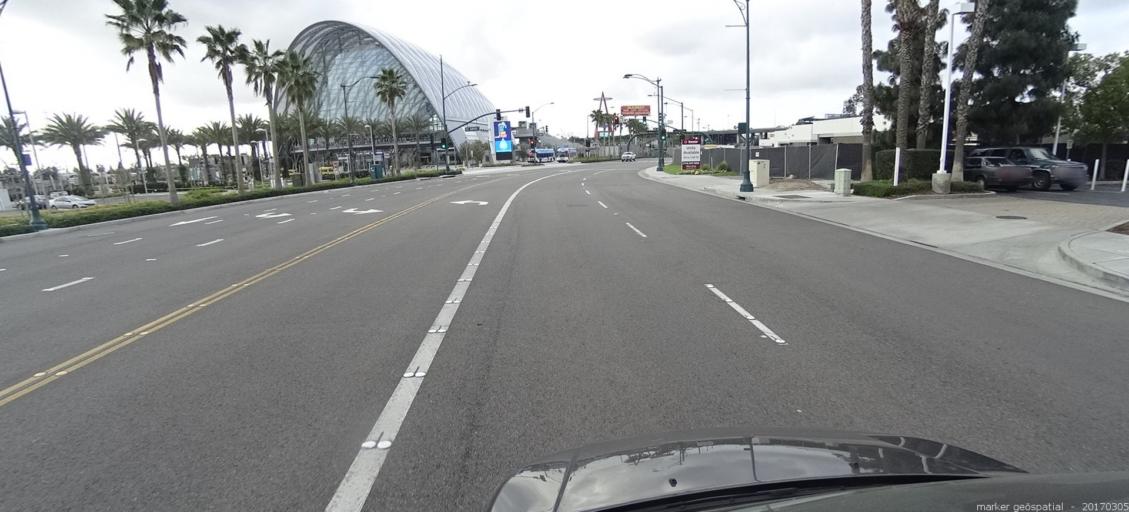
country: US
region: California
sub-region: Orange County
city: Orange
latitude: 33.8051
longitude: -117.8777
